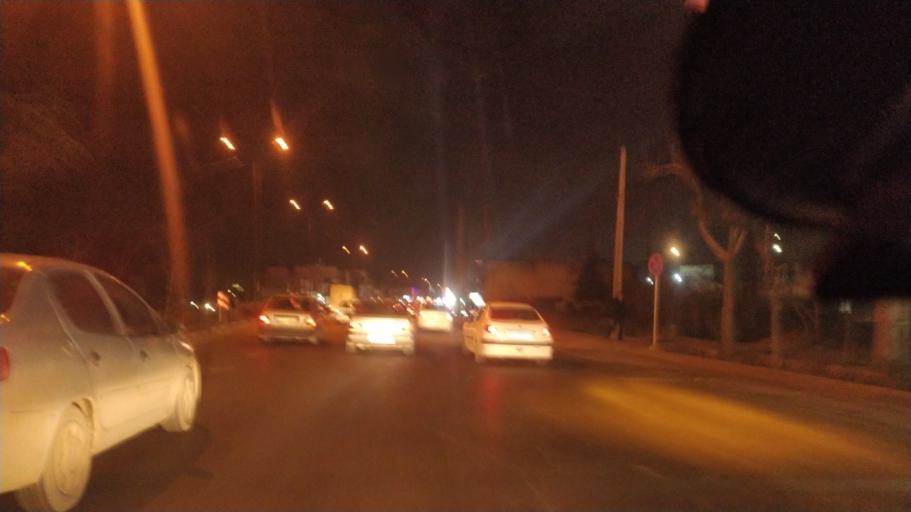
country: IR
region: Alborz
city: Karaj
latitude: 35.7851
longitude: 51.0060
